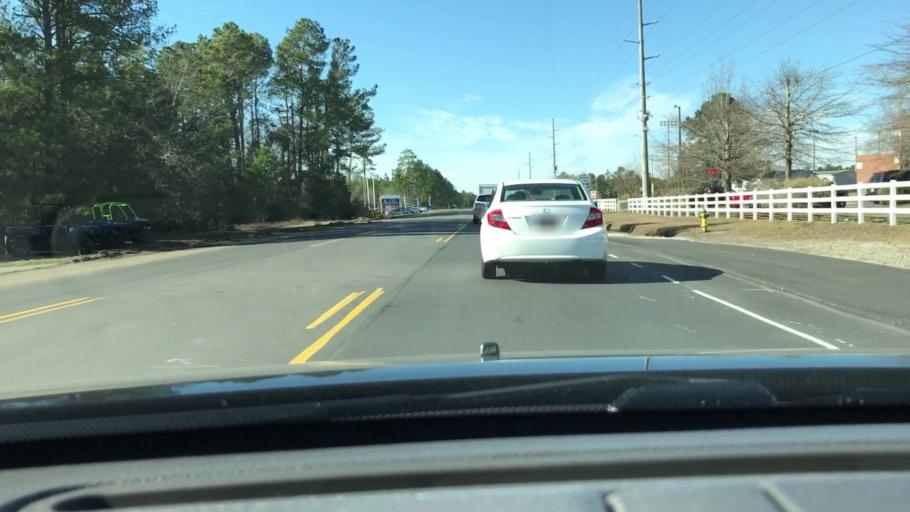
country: US
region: North Carolina
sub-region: Brunswick County
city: Shallotte
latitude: 33.9786
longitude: -78.4096
